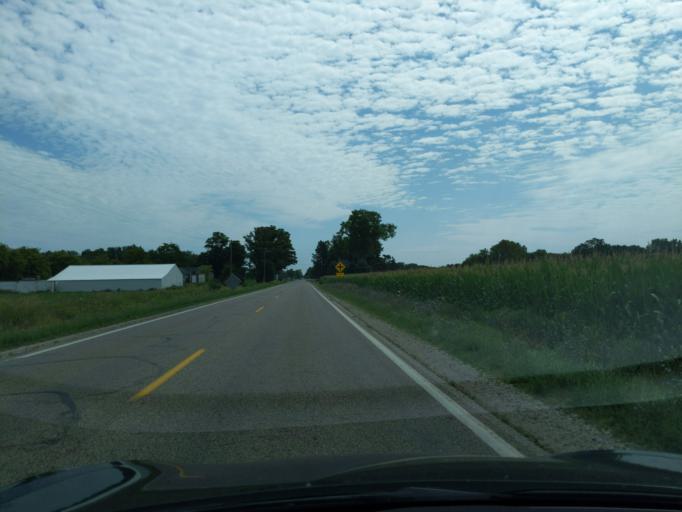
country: US
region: Michigan
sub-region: Gratiot County
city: Breckenridge
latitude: 43.2919
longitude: -84.4319
